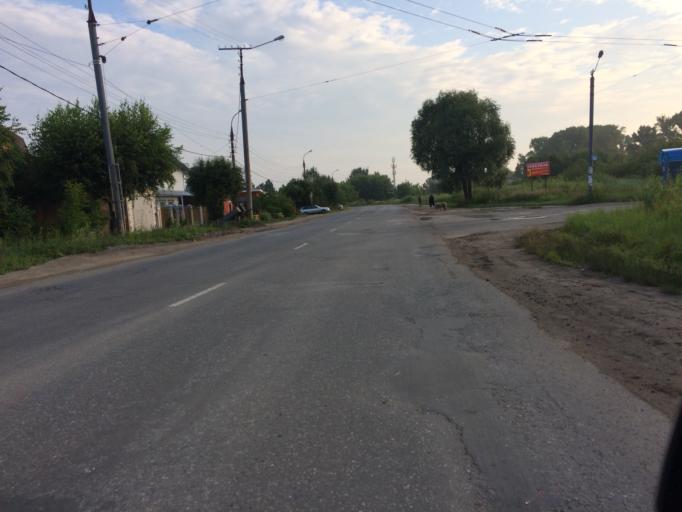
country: RU
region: Mariy-El
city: Yoshkar-Ola
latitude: 56.6460
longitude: 47.9544
